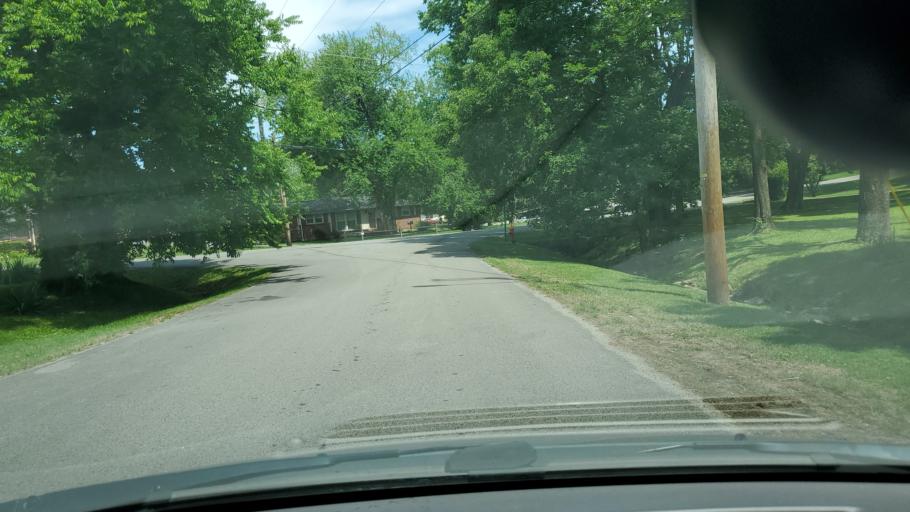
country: US
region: Tennessee
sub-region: Davidson County
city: Nashville
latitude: 36.2349
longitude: -86.7381
